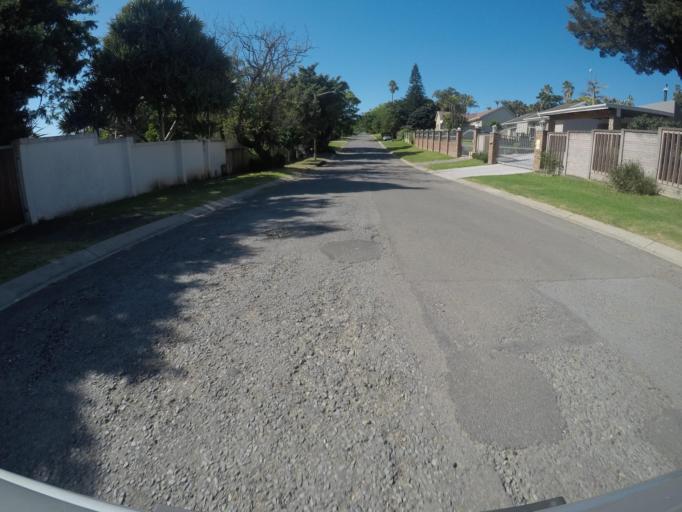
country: ZA
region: Eastern Cape
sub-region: Buffalo City Metropolitan Municipality
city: East London
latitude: -32.9483
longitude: 27.8993
